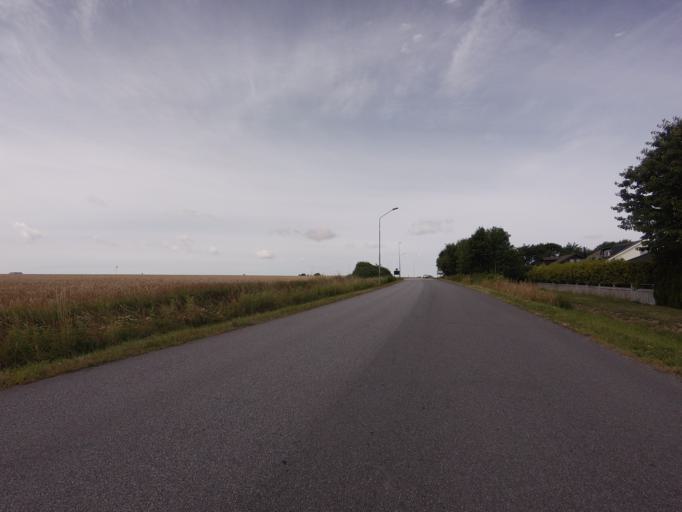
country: SE
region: Skane
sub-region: Simrishamns Kommun
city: Simrishamn
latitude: 55.5397
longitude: 14.3403
